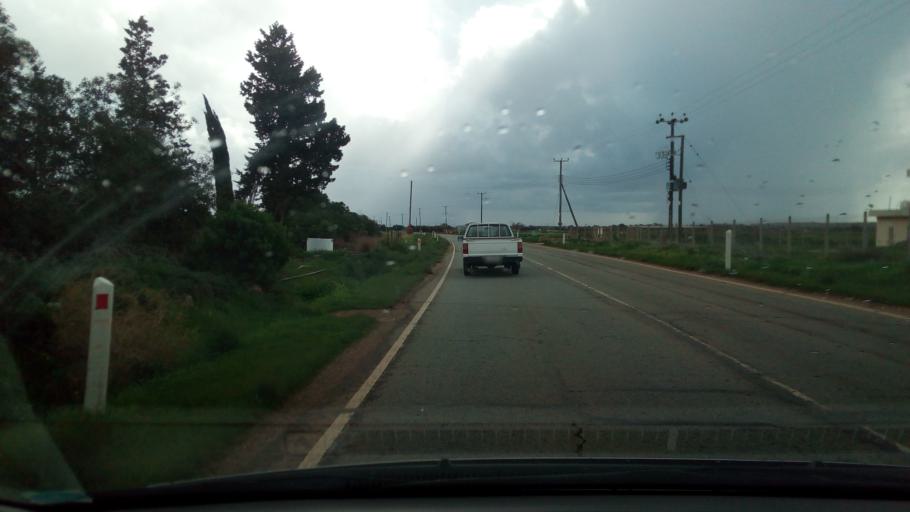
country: CY
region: Ammochostos
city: Liopetri
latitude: 34.9926
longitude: 33.8921
